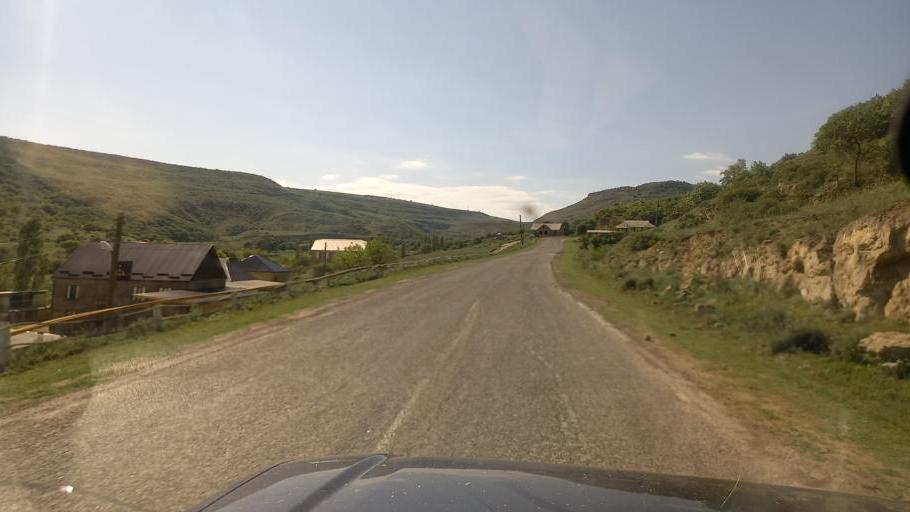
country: RU
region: Dagestan
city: Syrtych
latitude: 41.9489
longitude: 48.1513
